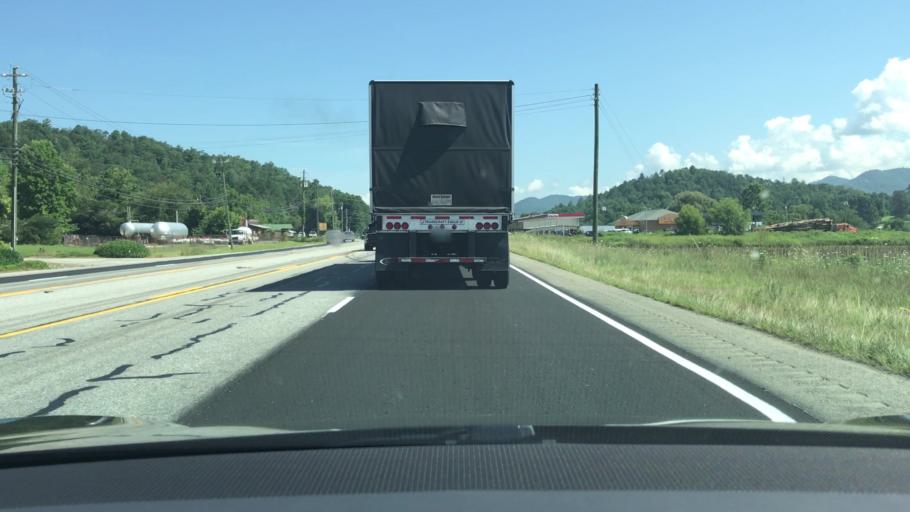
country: US
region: Georgia
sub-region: Rabun County
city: Mountain City
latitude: 34.9397
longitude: -83.3881
